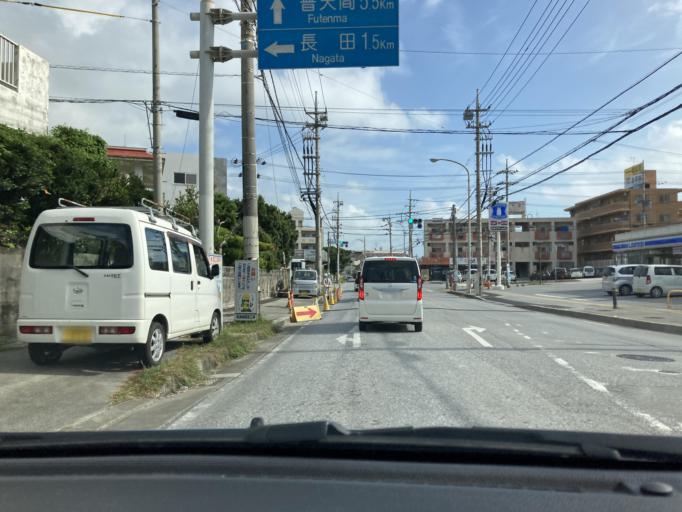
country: JP
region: Okinawa
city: Ginowan
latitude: 26.2539
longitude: 127.7738
